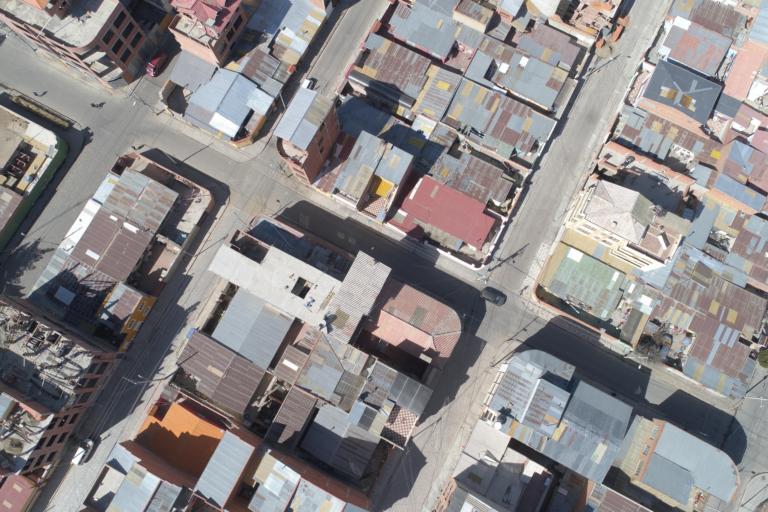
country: BO
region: La Paz
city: La Paz
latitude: -16.5281
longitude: -68.1538
